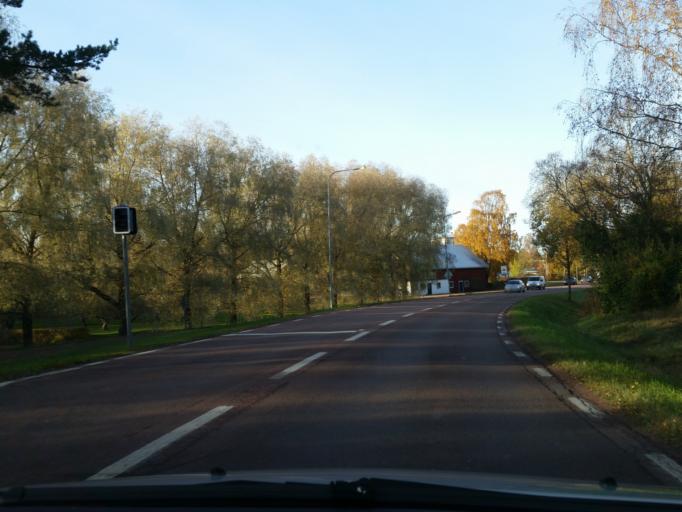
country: AX
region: Mariehamns stad
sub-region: Mariehamn
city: Mariehamn
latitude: 60.1076
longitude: 19.9312
